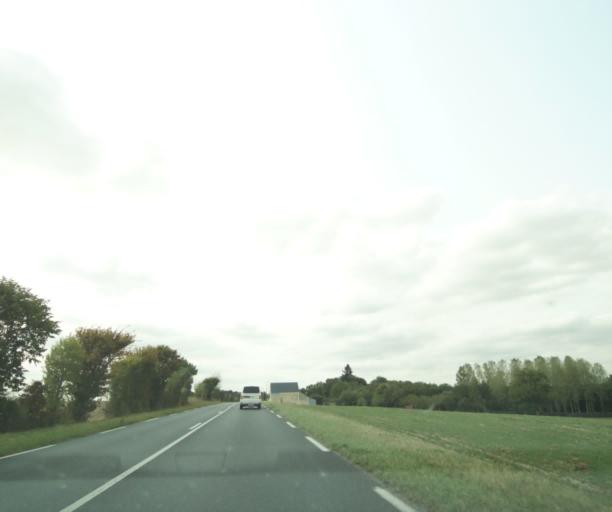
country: FR
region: Centre
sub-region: Departement de l'Indre
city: Chatillon-sur-Indre
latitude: 47.0007
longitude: 1.1479
